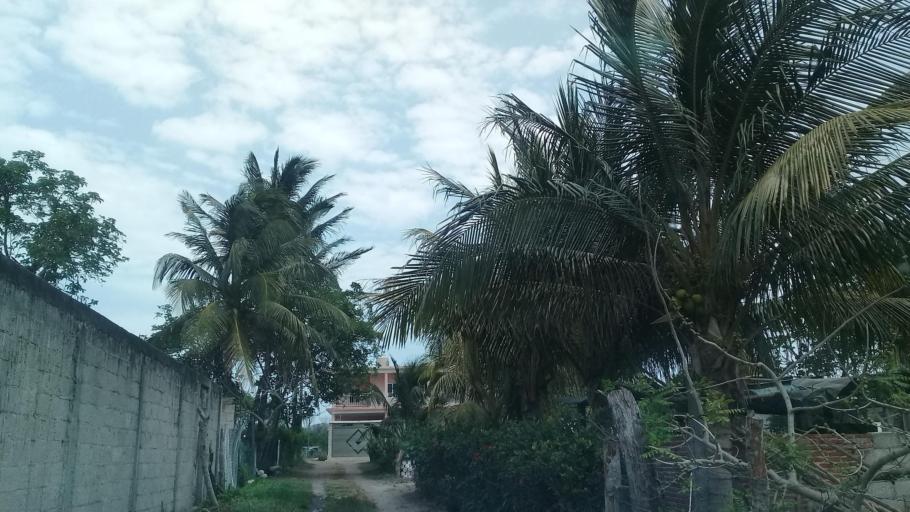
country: MX
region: Veracruz
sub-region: Veracruz
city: Delfino Victoria (Santa Fe)
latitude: 19.1737
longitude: -96.3026
